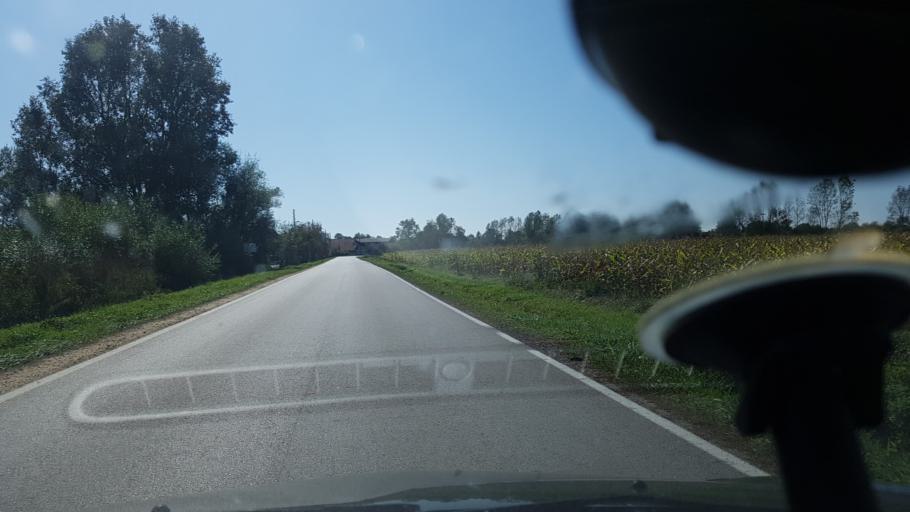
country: HR
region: Zagrebacka
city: Lupoglav
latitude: 45.6940
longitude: 16.3610
